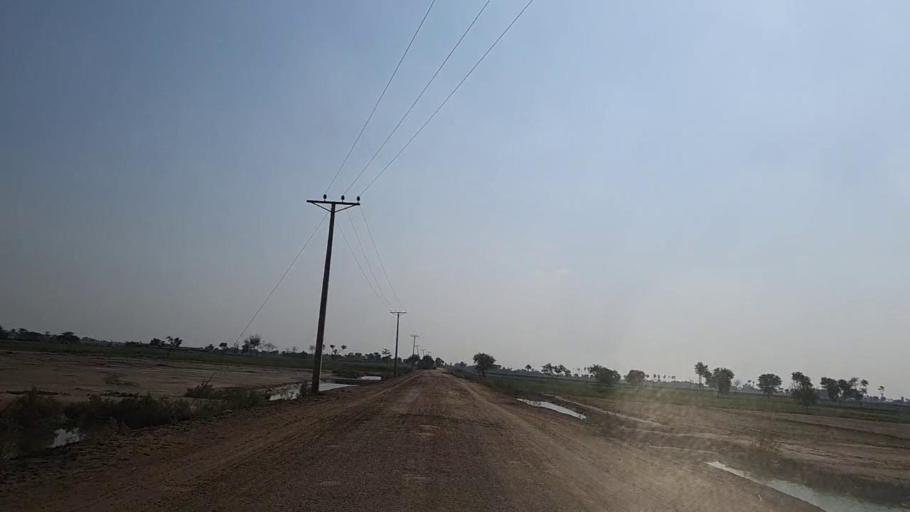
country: PK
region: Sindh
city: Daur
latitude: 26.4619
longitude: 68.2350
